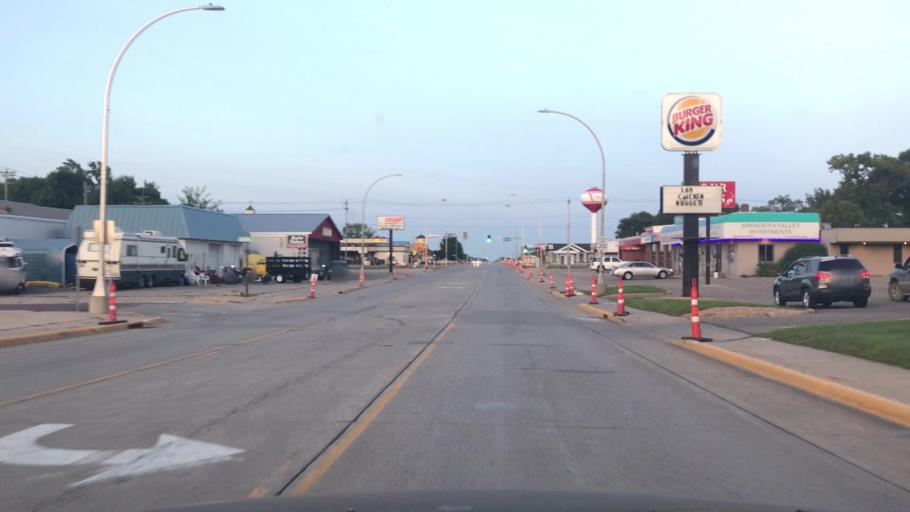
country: US
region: Minnesota
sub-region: Redwood County
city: Redwood Falls
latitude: 44.5414
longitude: -95.1118
